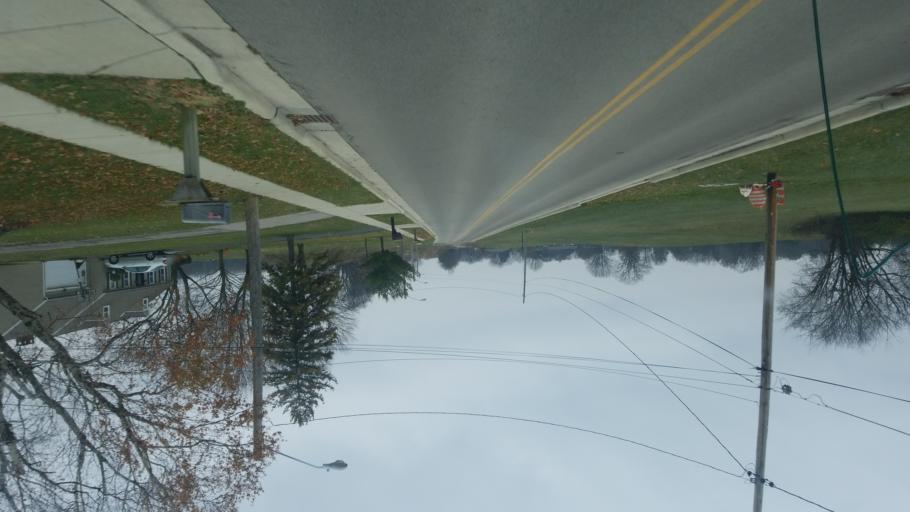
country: US
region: Ohio
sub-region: Crawford County
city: Galion
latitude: 40.7379
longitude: -82.8032
